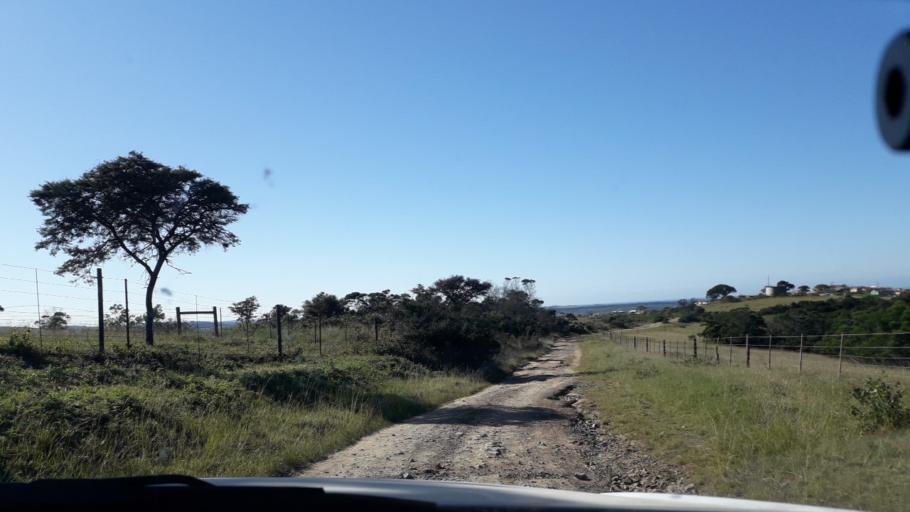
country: ZA
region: Eastern Cape
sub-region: Buffalo City Metropolitan Municipality
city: East London
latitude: -32.8409
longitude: 27.9781
